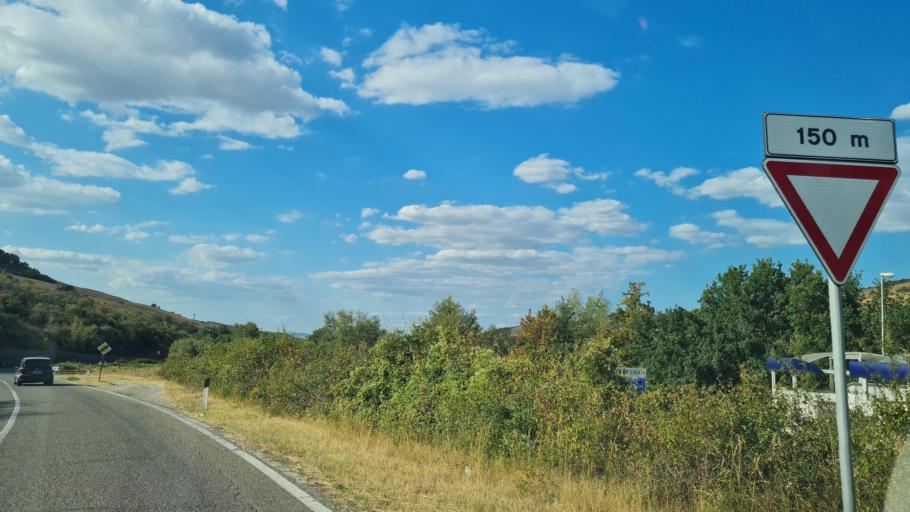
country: IT
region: Tuscany
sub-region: Provincia di Siena
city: Abbadia San Salvatore
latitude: 42.9398
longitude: 11.7113
